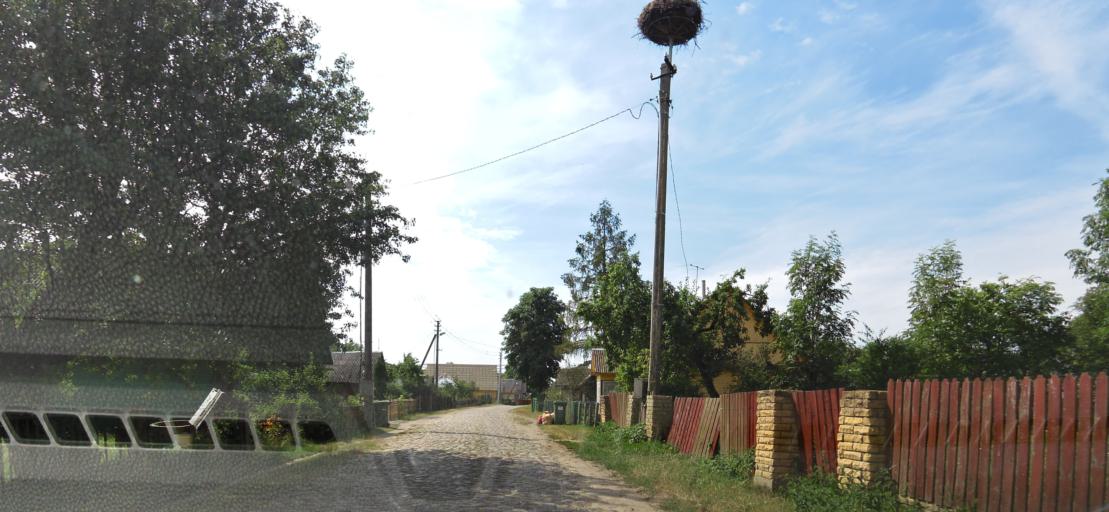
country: LT
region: Vilnius County
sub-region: Trakai
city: Rudiskes
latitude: 54.3648
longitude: 24.8455
